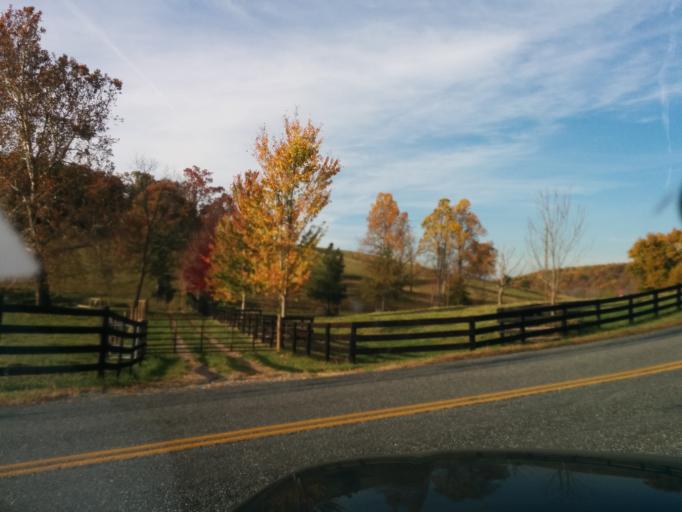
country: US
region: Virginia
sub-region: Rockbridge County
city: East Lexington
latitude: 37.8930
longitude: -79.3057
